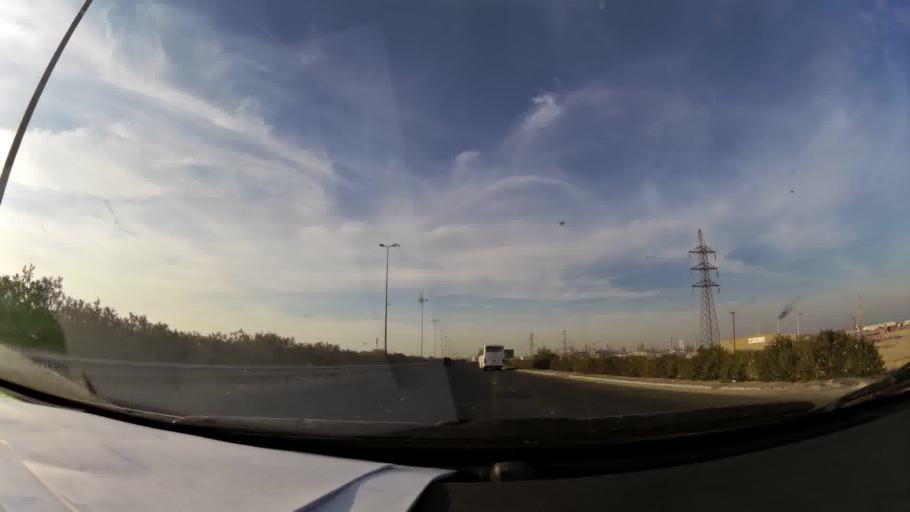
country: KW
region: Al Ahmadi
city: Al Fahahil
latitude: 28.9790
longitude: 48.1567
